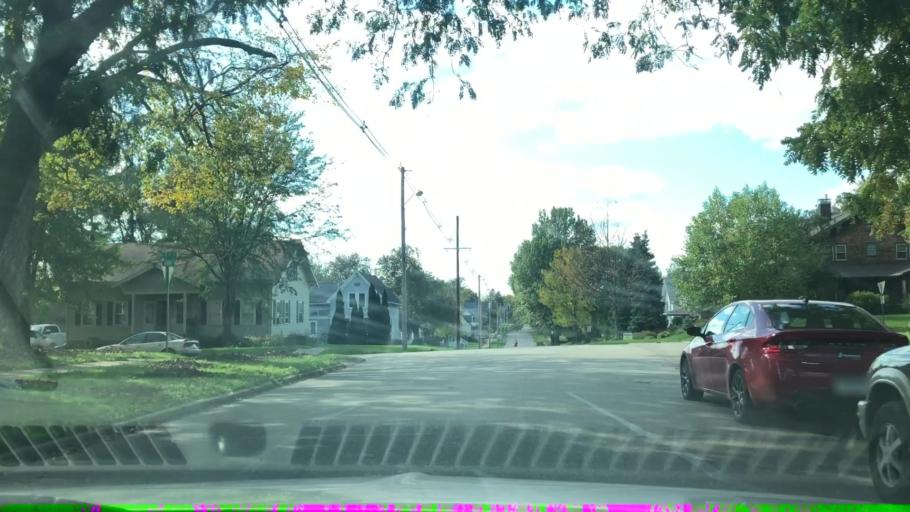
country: US
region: Iowa
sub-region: Marshall County
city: Marshalltown
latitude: 42.0540
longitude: -92.9206
